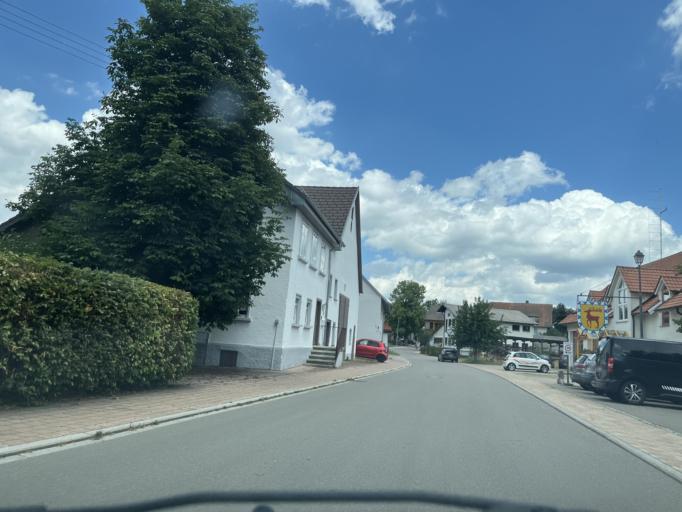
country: DE
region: Baden-Wuerttemberg
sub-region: Tuebingen Region
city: Leibertingen
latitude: 48.0429
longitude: 9.0143
